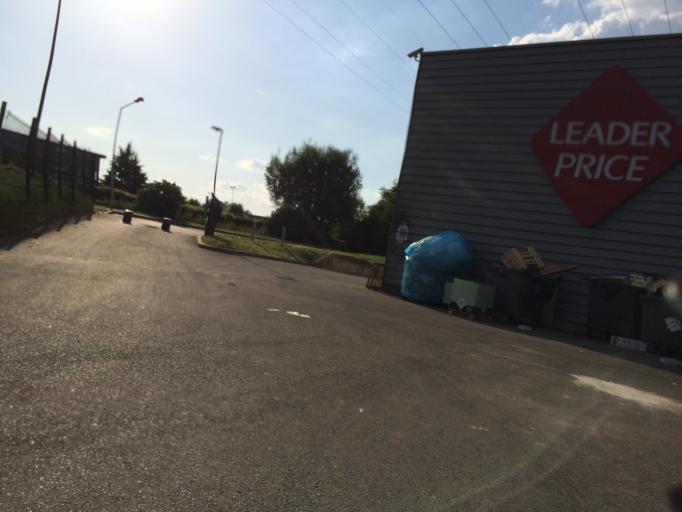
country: FR
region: Ile-de-France
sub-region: Departement de l'Essonne
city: Villabe
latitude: 48.6063
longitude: 2.4482
